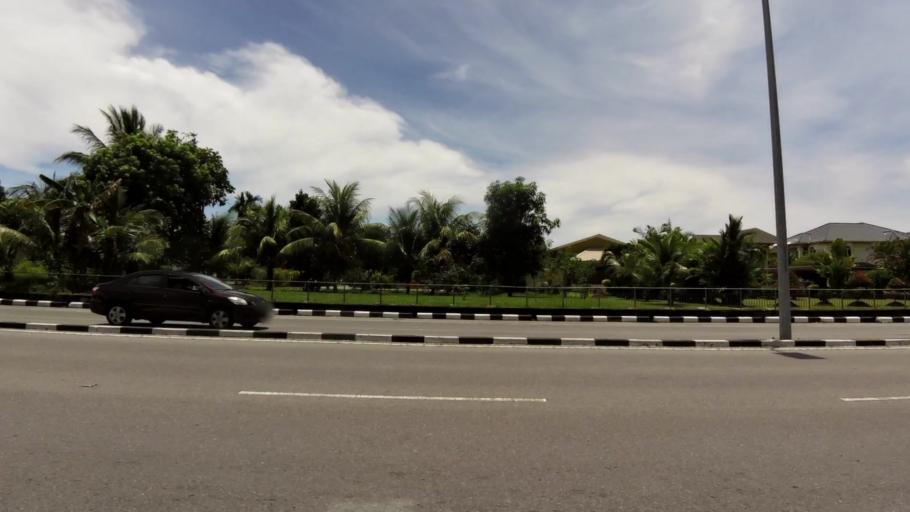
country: BN
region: Belait
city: Kuala Belait
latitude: 4.5824
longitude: 114.2355
